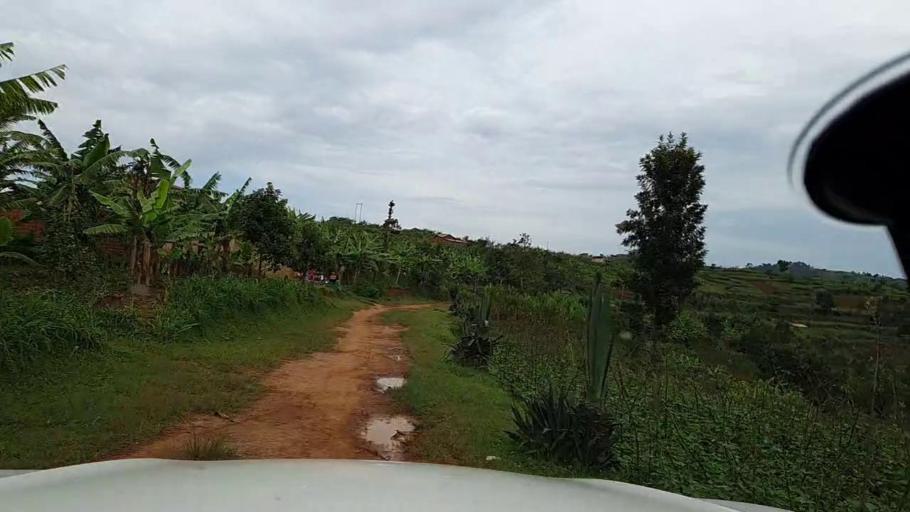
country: RW
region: Southern Province
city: Gitarama
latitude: -2.1158
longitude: 29.6423
